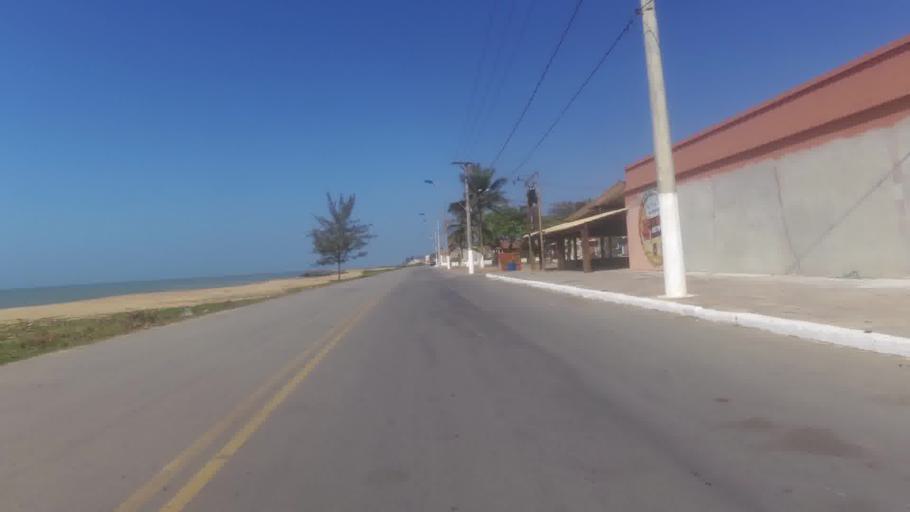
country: BR
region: Espirito Santo
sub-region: Marataizes
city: Marataizes
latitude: -21.0569
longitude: -40.8332
